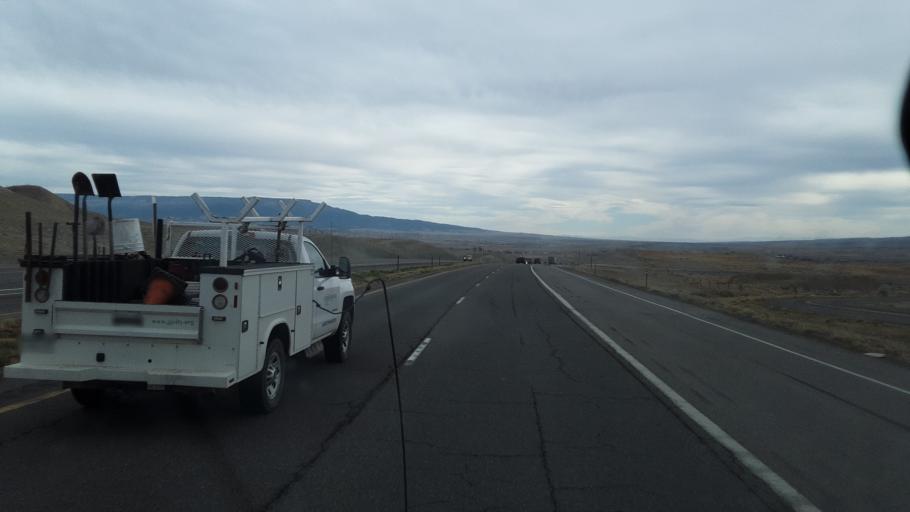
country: US
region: Colorado
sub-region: Mesa County
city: Fruitvale
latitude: 39.0112
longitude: -108.4701
